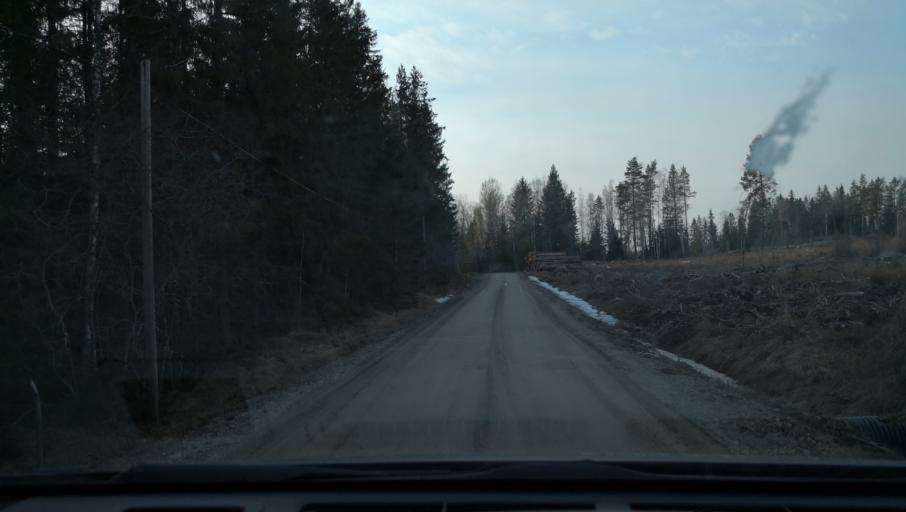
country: SE
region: OErebro
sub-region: Orebro Kommun
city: Hovsta
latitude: 59.3823
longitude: 15.2811
